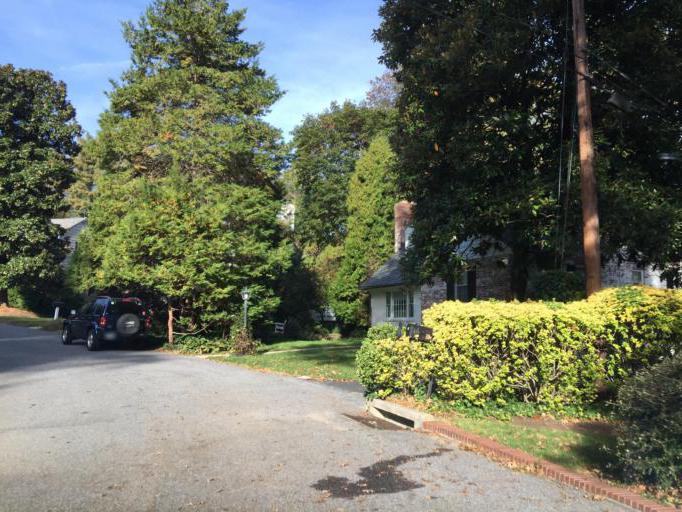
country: US
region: Maryland
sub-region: Baltimore County
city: Towson
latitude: 39.3879
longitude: -76.6264
